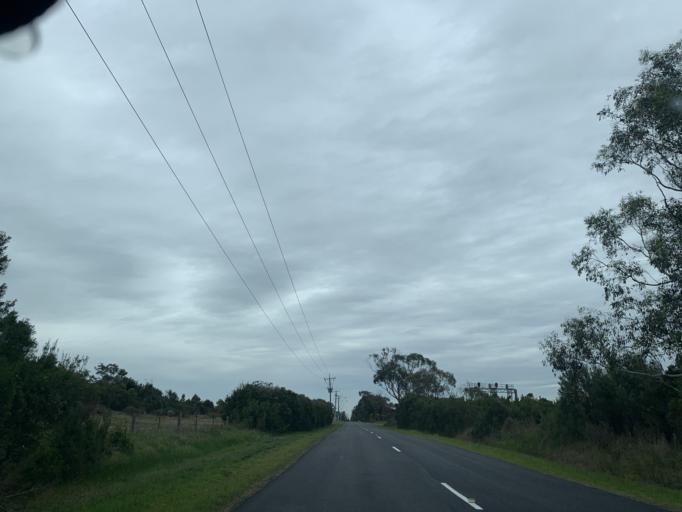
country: AU
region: Victoria
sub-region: Cardinia
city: Garfield
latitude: -38.0845
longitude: 145.6146
